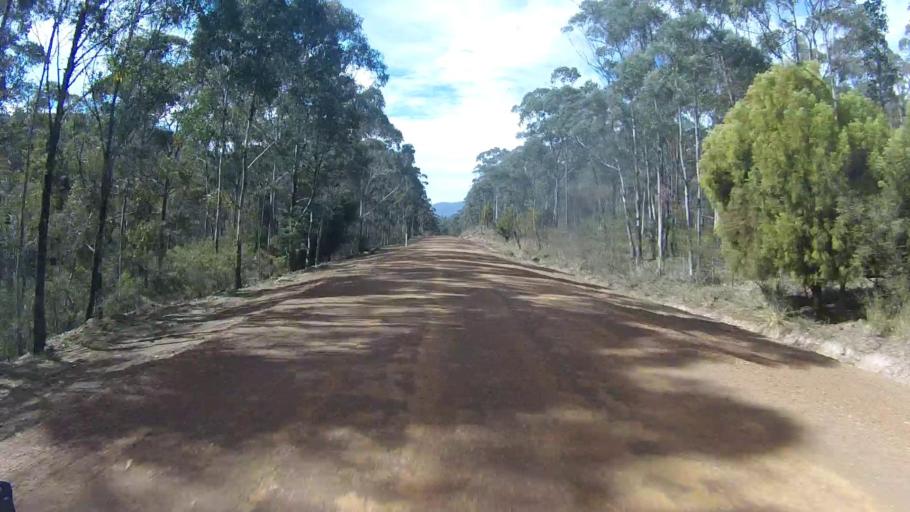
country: AU
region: Tasmania
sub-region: Sorell
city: Sorell
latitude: -42.6178
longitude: 147.9008
